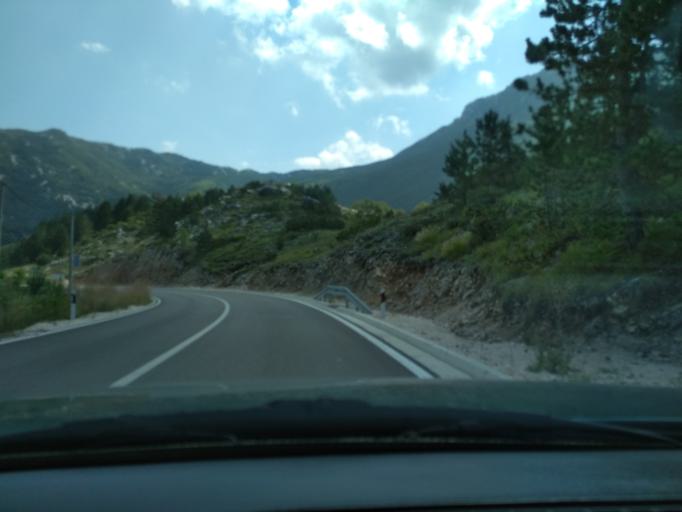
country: ME
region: Kotor
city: Kotor
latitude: 42.4279
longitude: 18.8167
